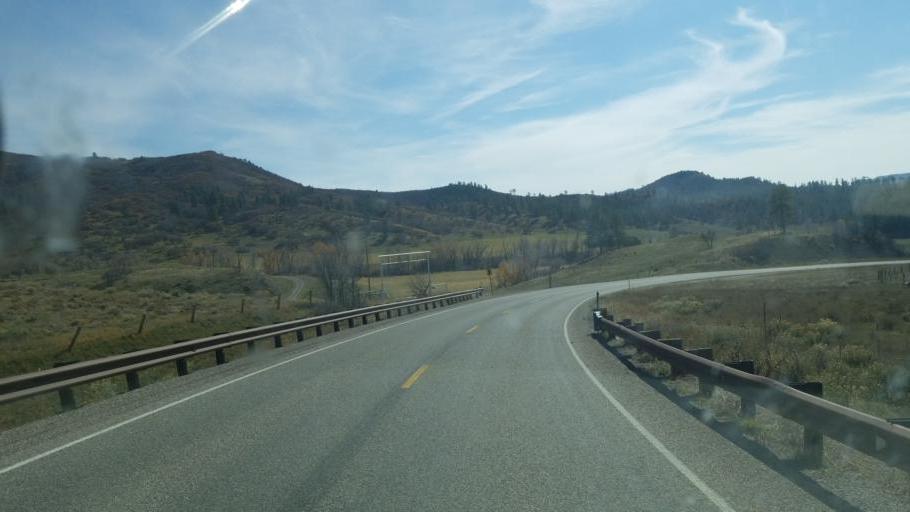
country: US
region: New Mexico
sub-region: Rio Arriba County
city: Dulce
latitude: 37.0730
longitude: -106.8264
